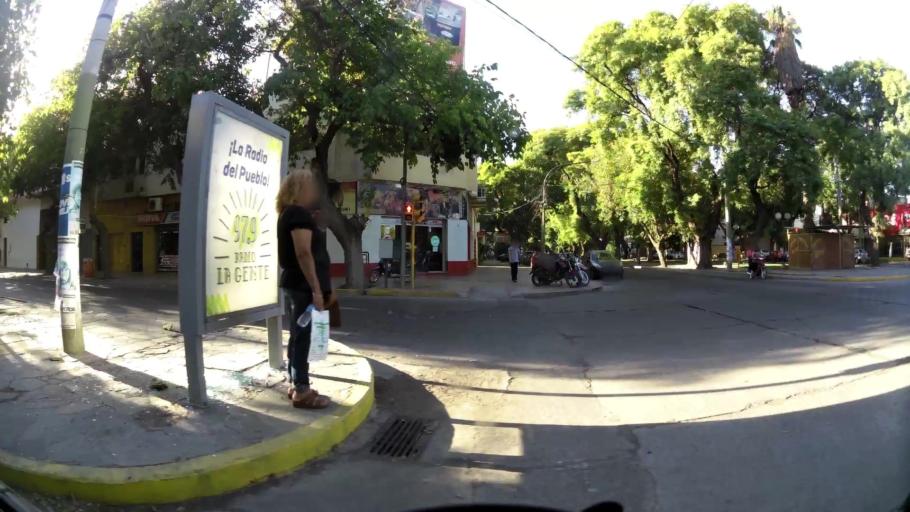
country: AR
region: San Juan
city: San Juan
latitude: -31.5335
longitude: -68.5155
